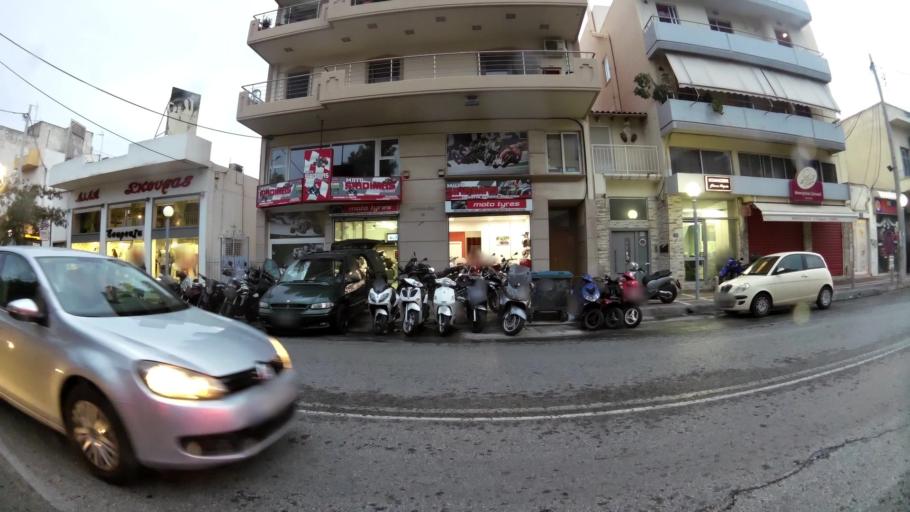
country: GR
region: Attica
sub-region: Nomarchia Athinas
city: Ymittos
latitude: 37.9469
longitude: 23.7466
